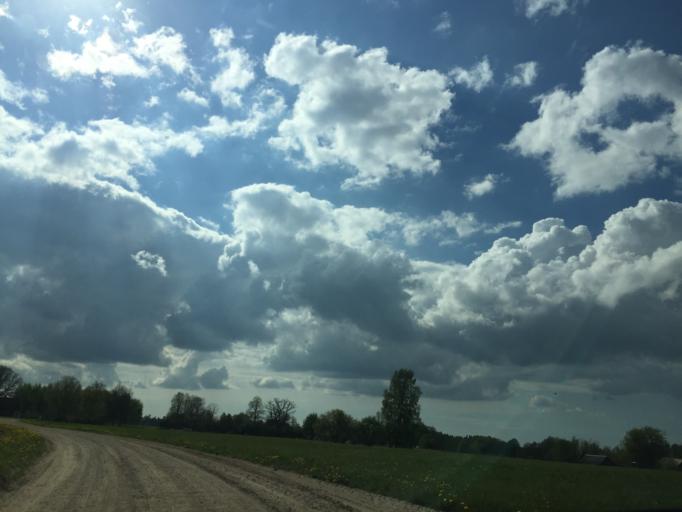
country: LV
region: Sigulda
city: Sigulda
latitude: 57.2935
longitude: 24.8230
